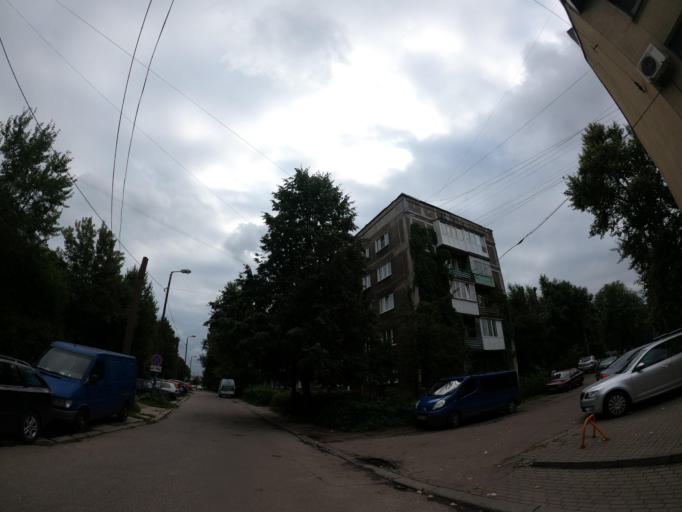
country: RU
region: Kaliningrad
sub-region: Gorod Kaliningrad
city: Kaliningrad
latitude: 54.6989
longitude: 20.5131
